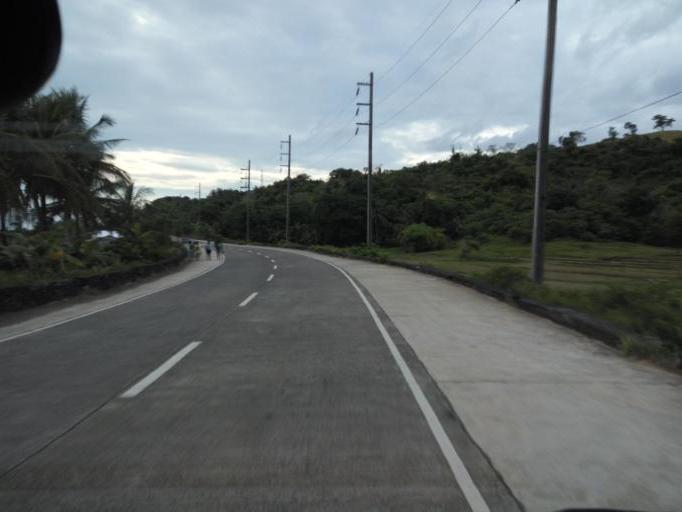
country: PH
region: Cagayan Valley
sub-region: Province of Cagayan
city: Casambalangan
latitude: 18.3935
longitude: 122.1374
